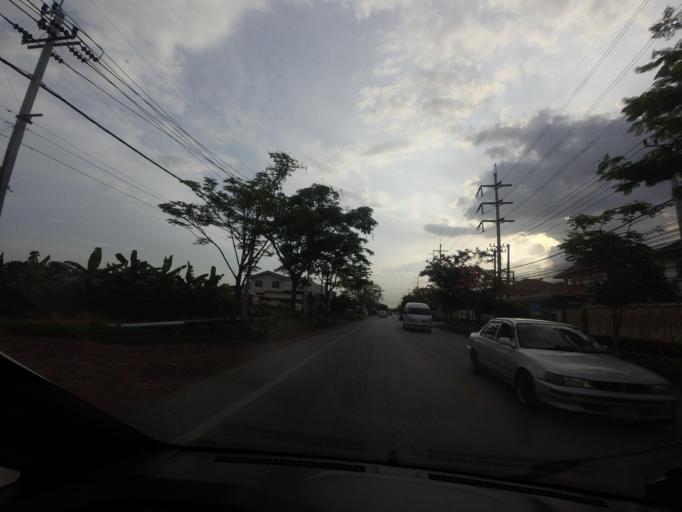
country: TH
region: Bangkok
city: Nong Chok
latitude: 13.8560
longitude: 100.8235
